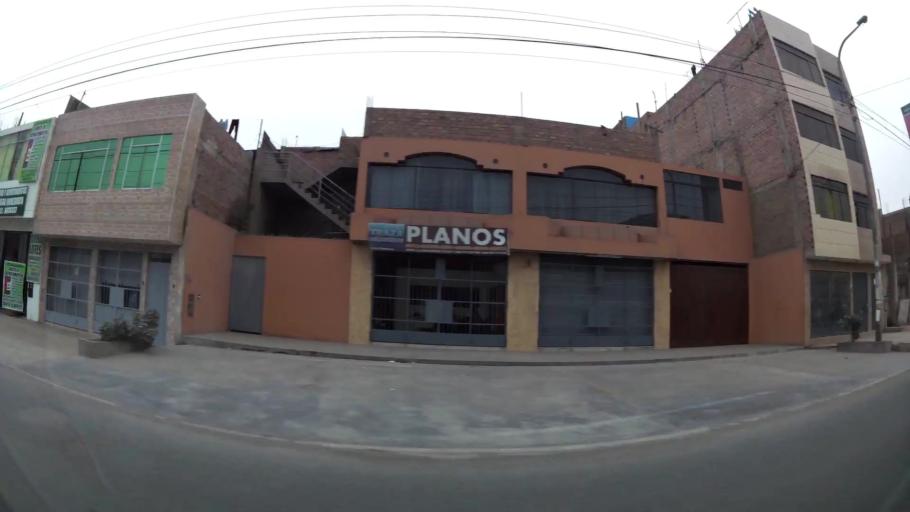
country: PE
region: Lima
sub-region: Lima
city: Urb. Santo Domingo
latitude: -11.8833
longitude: -77.0338
